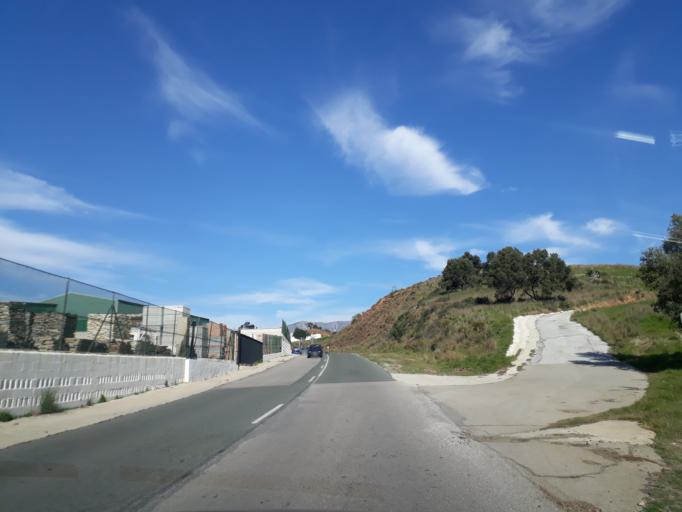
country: ES
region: Andalusia
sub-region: Provincia de Malaga
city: Fuengirola
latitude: 36.5178
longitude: -4.6847
